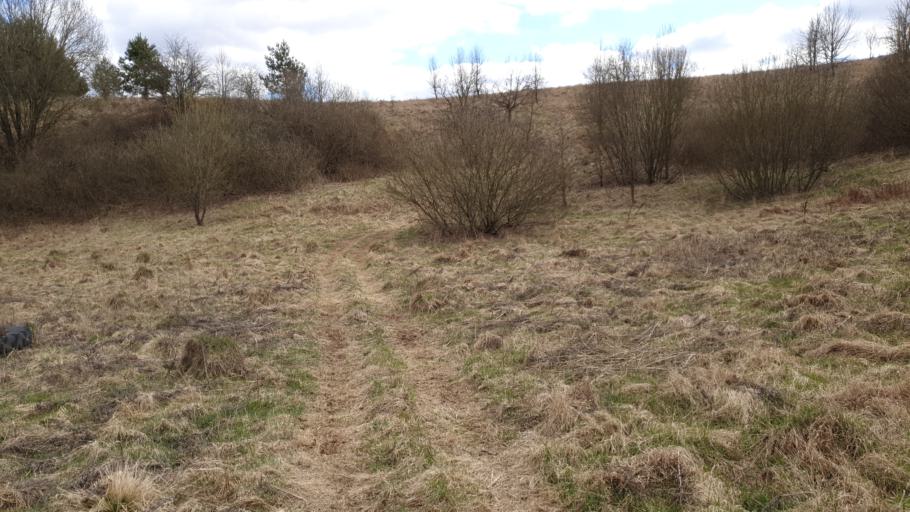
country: LT
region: Vilnius County
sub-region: Vilniaus Rajonas
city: Vievis
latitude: 54.6426
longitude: 24.7317
